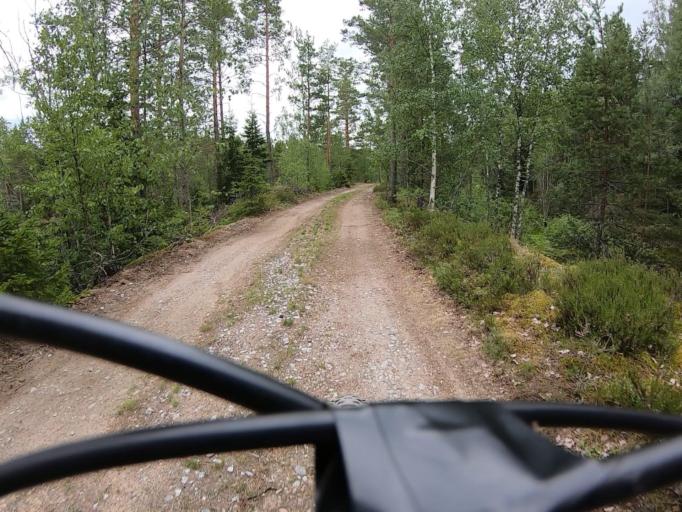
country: FI
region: Varsinais-Suomi
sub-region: Vakka-Suomi
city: Uusikaupunki
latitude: 60.8538
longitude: 21.4205
